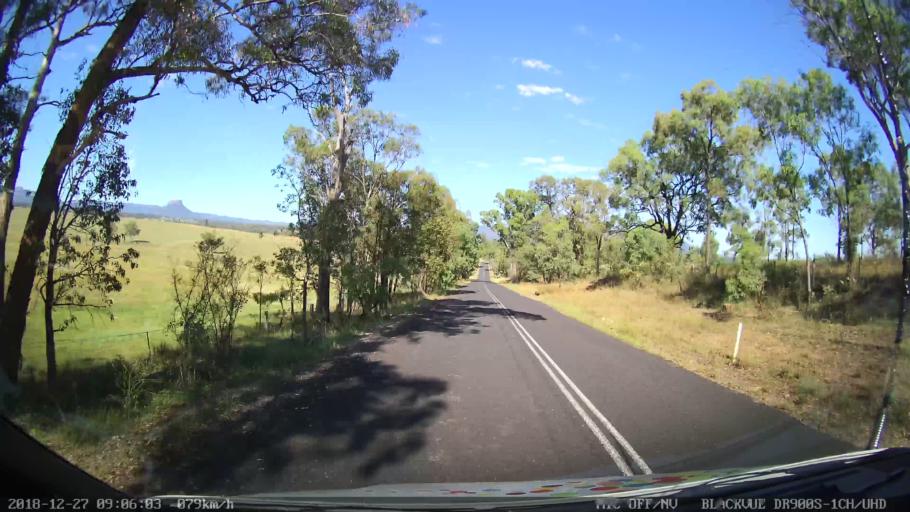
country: AU
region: New South Wales
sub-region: Lithgow
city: Portland
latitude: -33.1199
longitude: 150.1722
